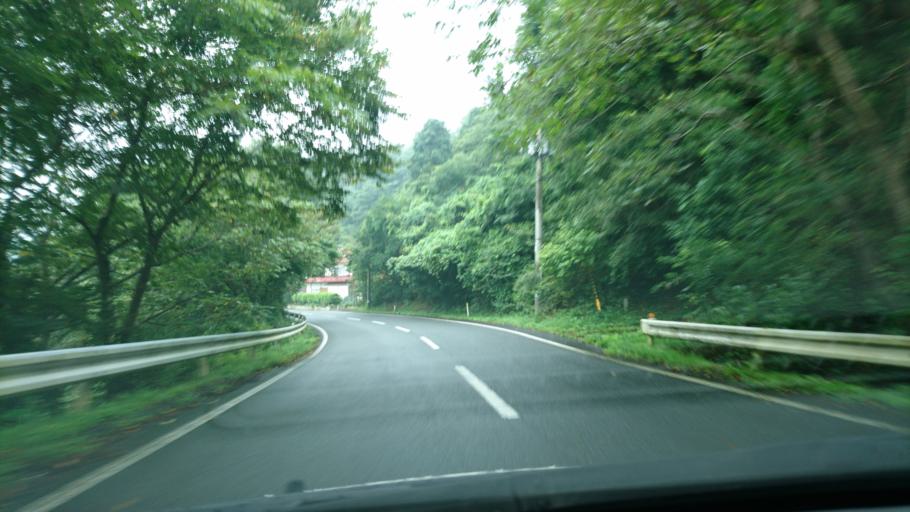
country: JP
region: Iwate
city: Ichinoseki
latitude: 38.8932
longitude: 141.2669
